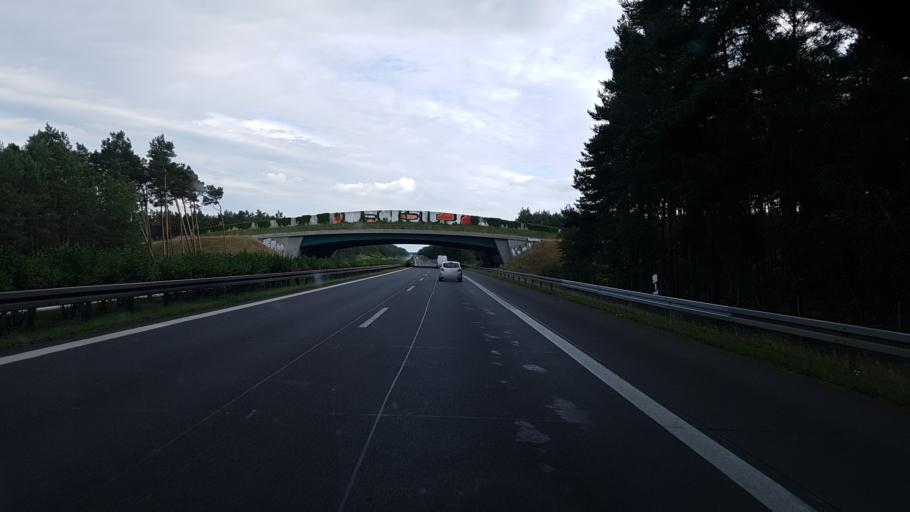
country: DE
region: Brandenburg
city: Teupitz
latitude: 52.1109
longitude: 13.6463
